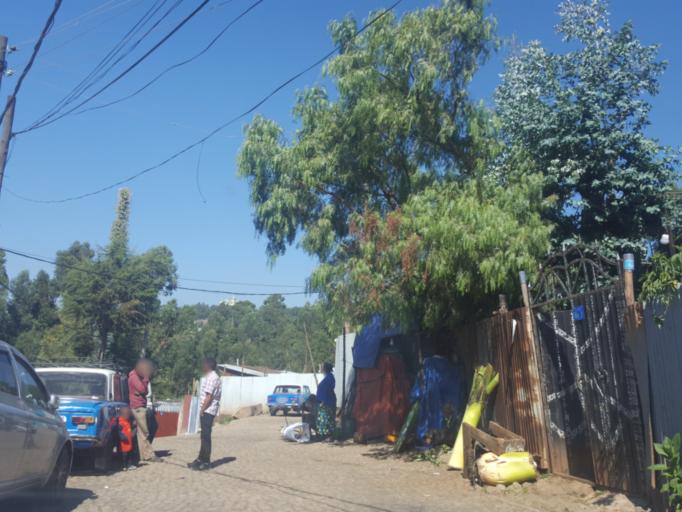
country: ET
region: Adis Abeba
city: Addis Ababa
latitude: 9.0620
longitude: 38.7481
